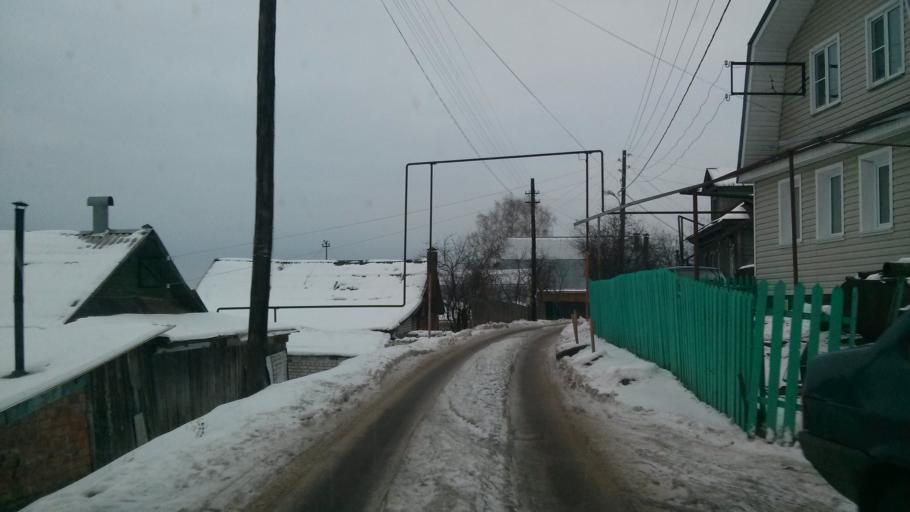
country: RU
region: Nizjnij Novgorod
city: Afonino
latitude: 56.2977
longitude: 44.0999
